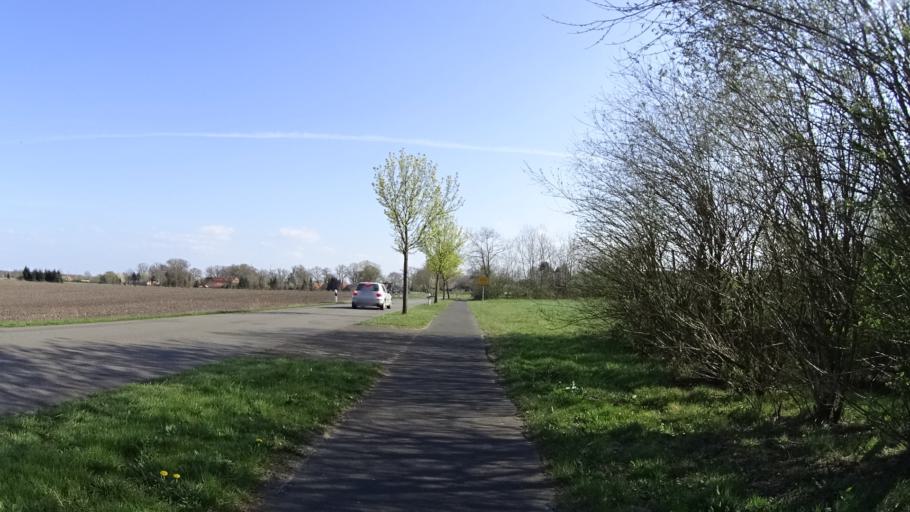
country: DE
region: Lower Saxony
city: Dorpen
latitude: 52.9421
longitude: 7.3173
